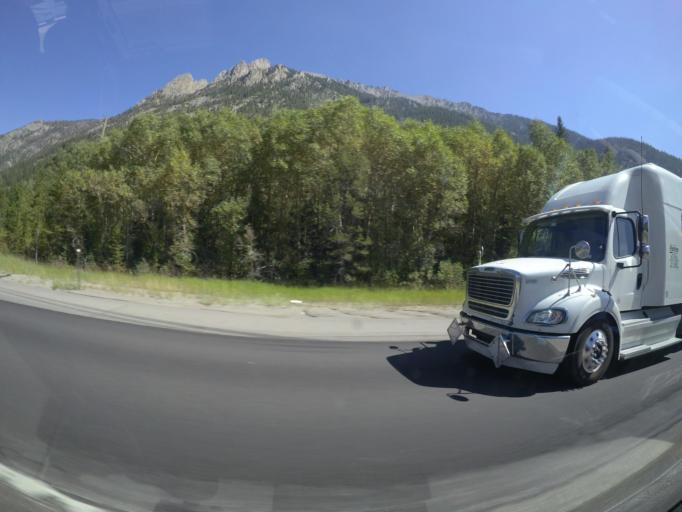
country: US
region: Colorado
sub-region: Summit County
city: Frisco
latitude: 39.5453
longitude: -106.1406
